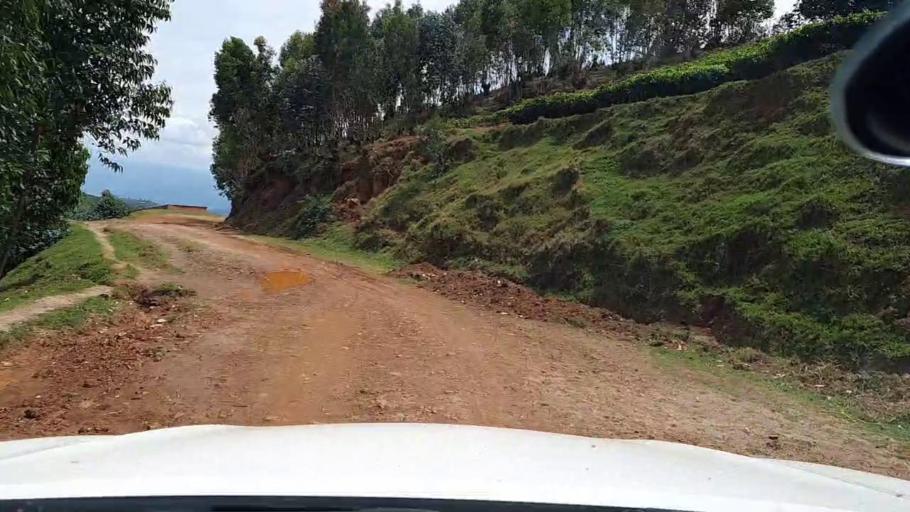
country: RW
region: Western Province
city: Kibuye
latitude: -2.1656
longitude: 29.3998
